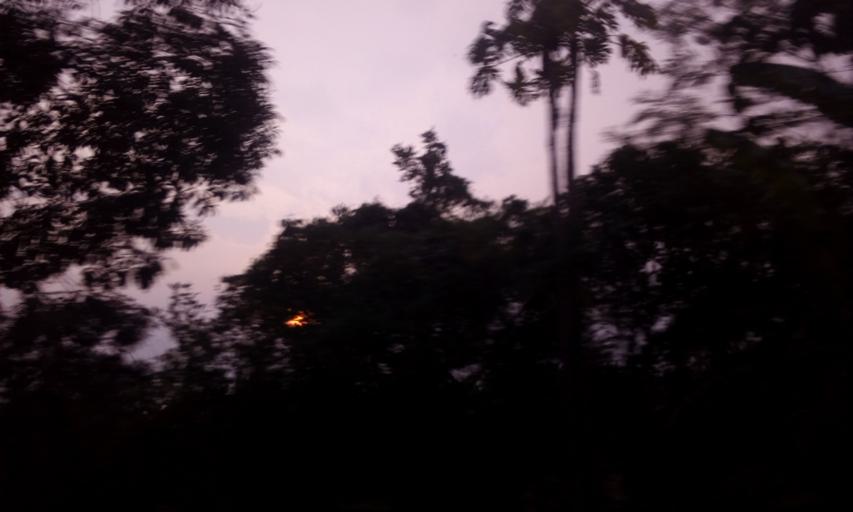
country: TH
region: Bangkok
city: Nong Chok
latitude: 13.9241
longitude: 100.8922
